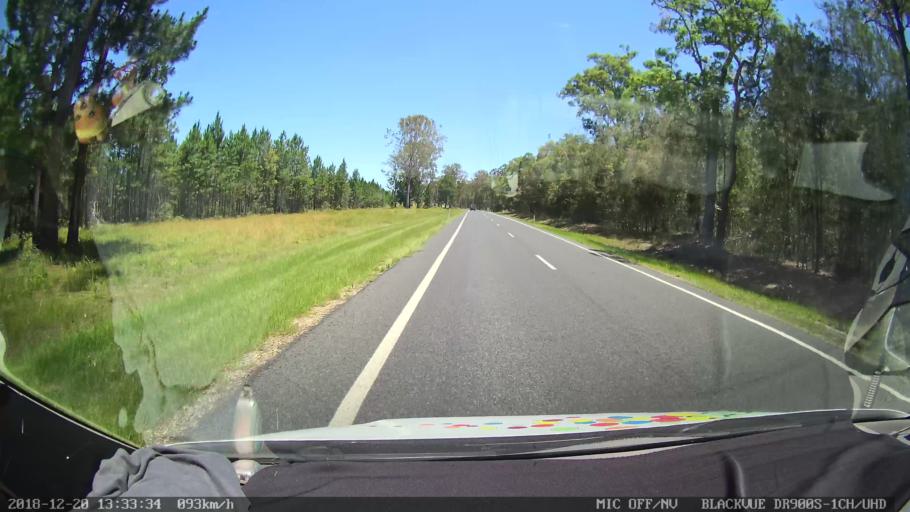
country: AU
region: New South Wales
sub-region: Clarence Valley
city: Gordon
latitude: -29.2472
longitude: 152.9860
